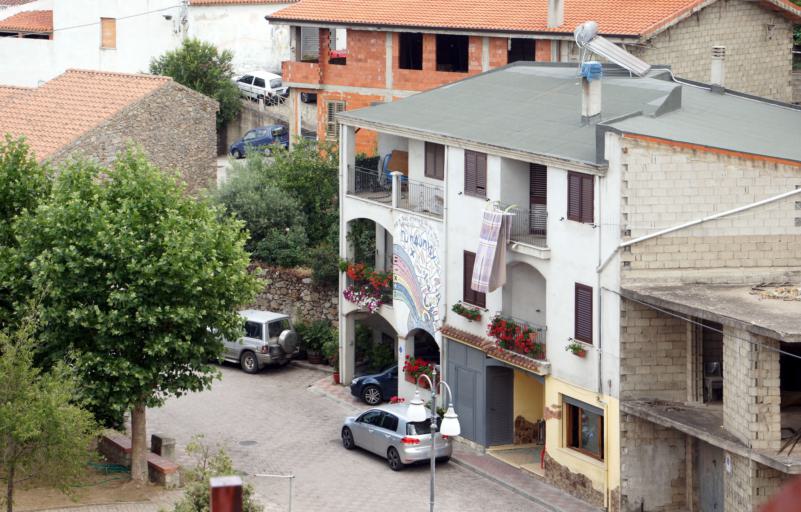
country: IT
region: Sardinia
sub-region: Provincia di Nuoro
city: Orgosolo
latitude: 40.2038
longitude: 9.3539
